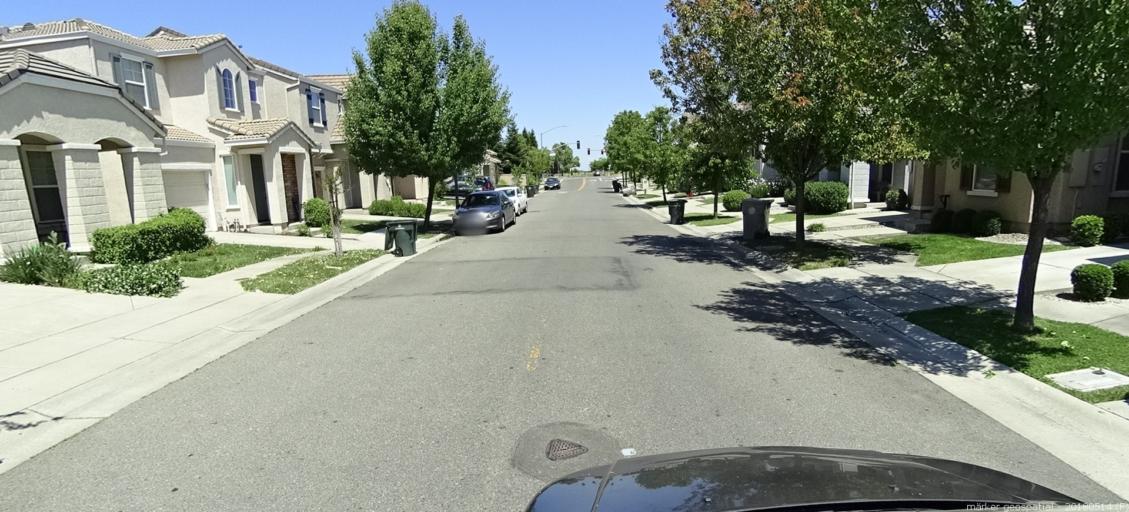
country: US
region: California
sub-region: Yolo County
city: West Sacramento
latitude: 38.6266
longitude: -121.5222
